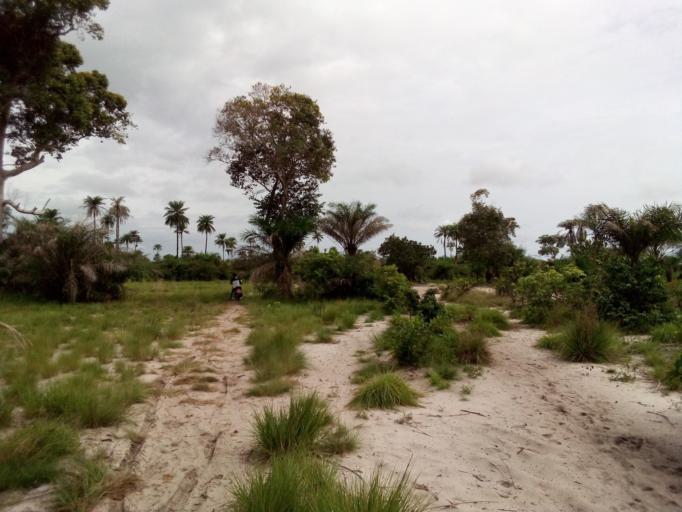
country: SL
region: Southern Province
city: Bonthe
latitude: 7.5168
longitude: -12.5700
